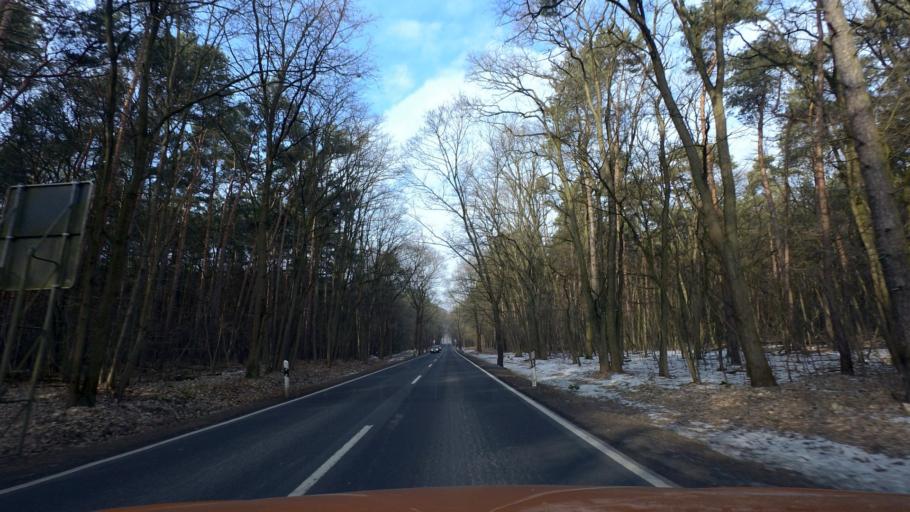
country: DE
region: Brandenburg
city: Am Mellensee
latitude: 52.2280
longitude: 13.4021
